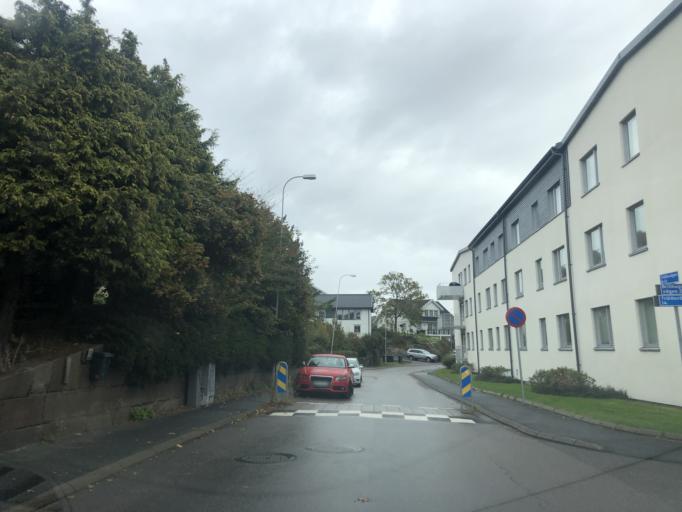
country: SE
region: Vaestra Goetaland
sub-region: Goteborg
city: Majorna
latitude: 57.6702
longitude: 11.8989
